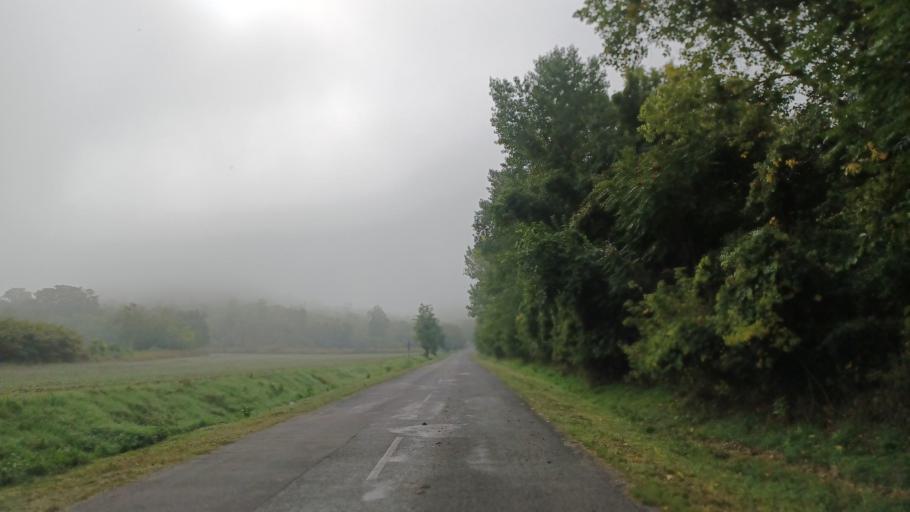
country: HU
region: Tolna
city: Pincehely
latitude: 46.6857
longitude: 18.4615
